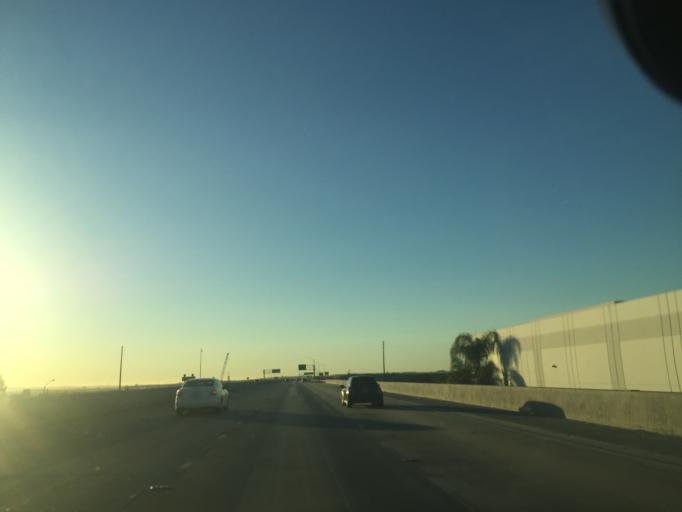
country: MX
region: Baja California
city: Tijuana
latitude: 32.5641
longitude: -116.9392
